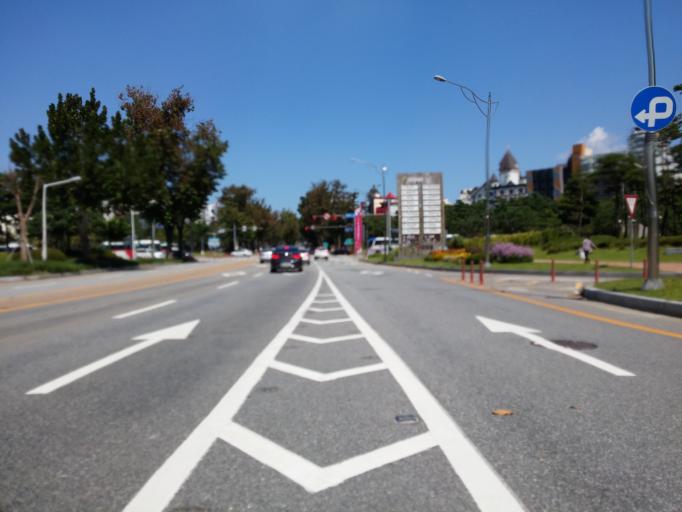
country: KR
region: Chungcheongbuk-do
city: Cheongju-si
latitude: 36.6277
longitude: 127.4277
